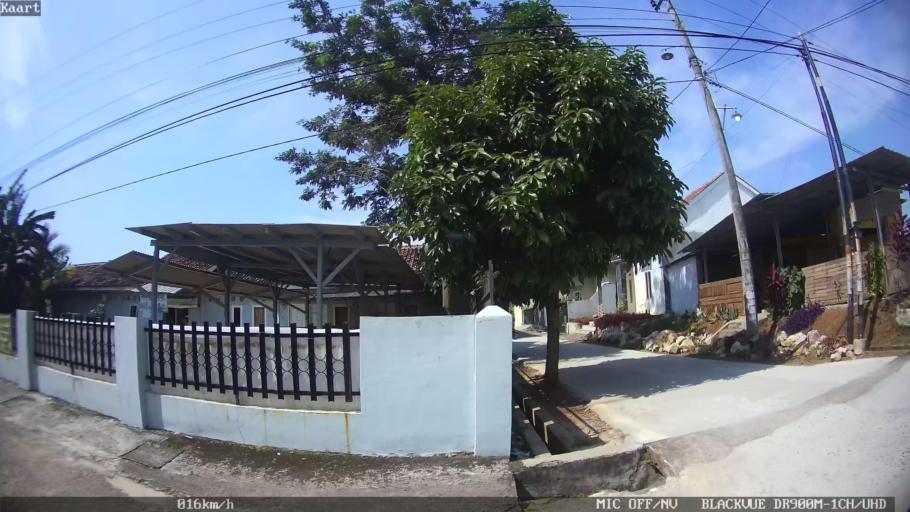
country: ID
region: Lampung
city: Kedaton
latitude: -5.3706
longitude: 105.2462
